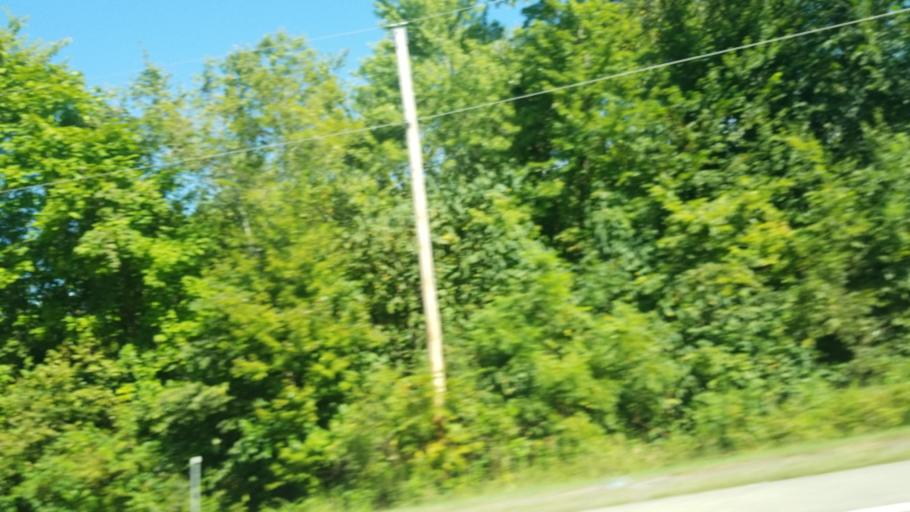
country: US
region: Illinois
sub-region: Williamson County
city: Marion
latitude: 37.7572
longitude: -88.9328
